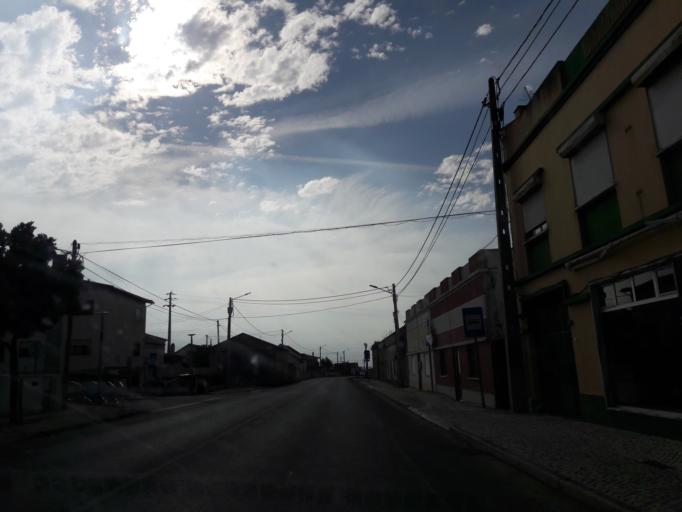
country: PT
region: Leiria
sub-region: Peniche
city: Atouguia da Baleia
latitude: 39.3401
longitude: -9.3292
